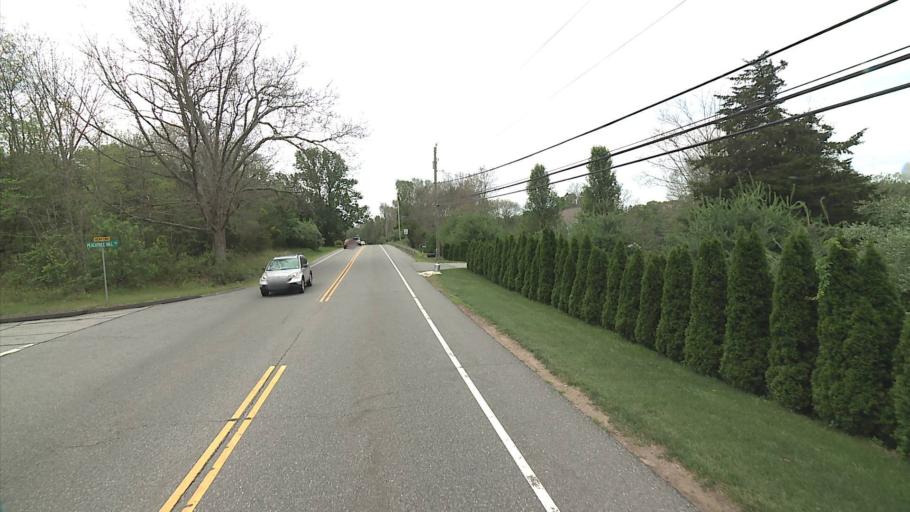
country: US
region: Connecticut
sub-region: New London County
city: Ledyard Center
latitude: 41.4171
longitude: -72.0183
